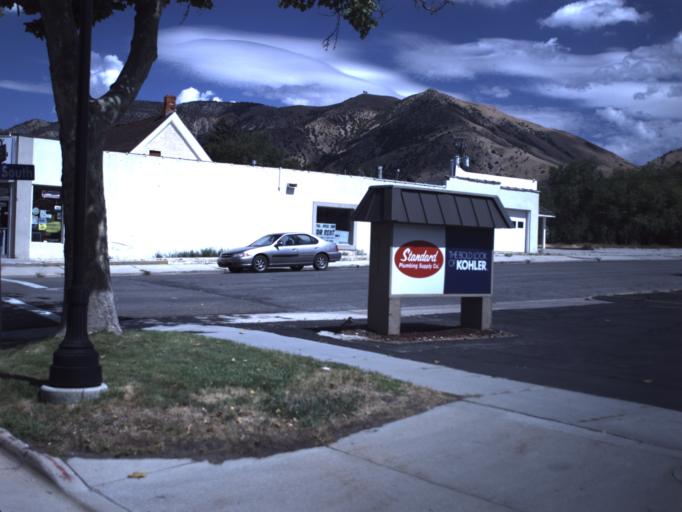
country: US
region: Utah
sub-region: Box Elder County
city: Brigham City
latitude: 41.5006
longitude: -112.0159
